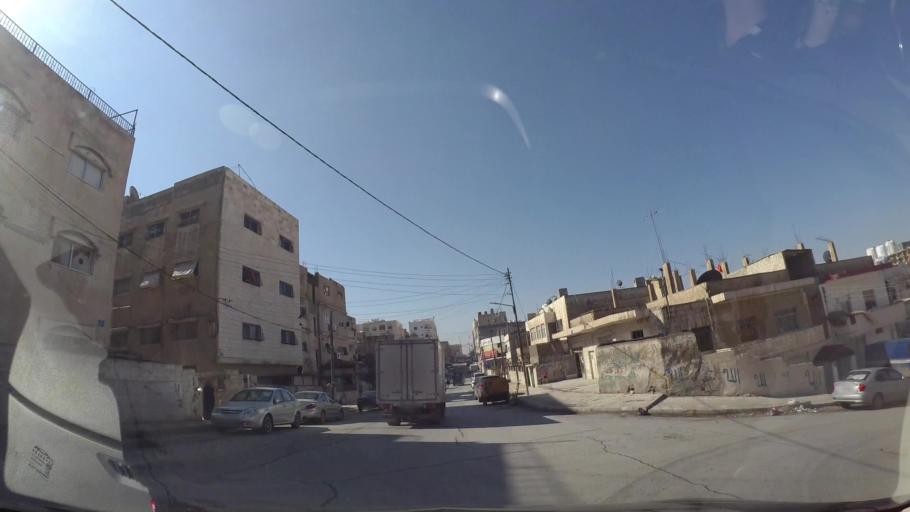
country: JO
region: Amman
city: Amman
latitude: 31.9857
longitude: 35.9880
